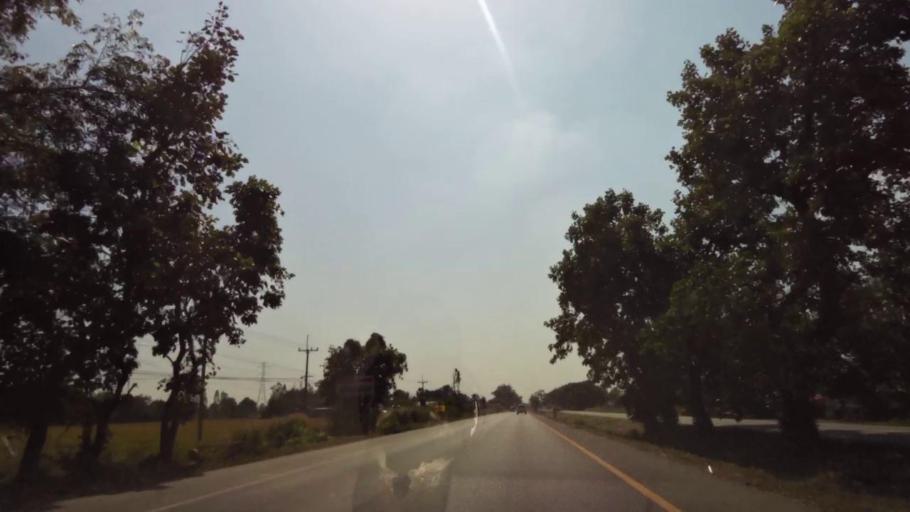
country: TH
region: Phichit
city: Wachira Barami
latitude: 16.3896
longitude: 100.1385
